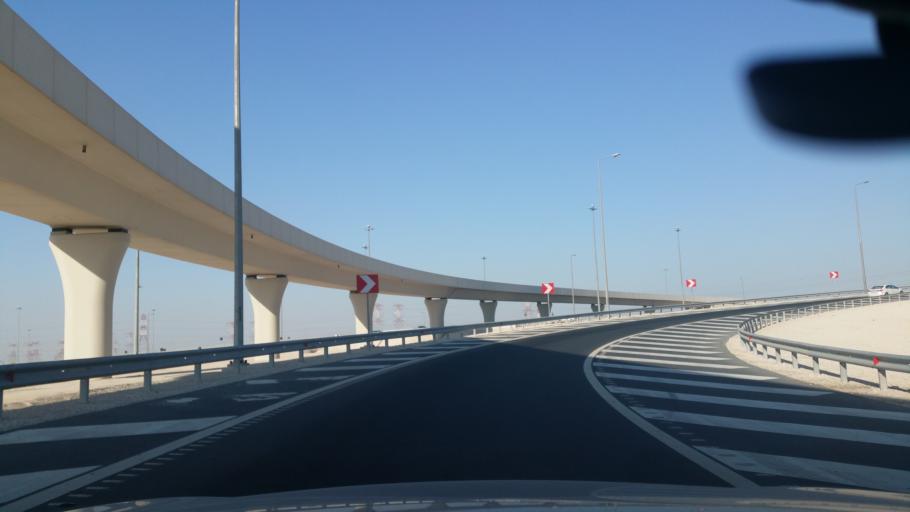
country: QA
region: Baladiyat ar Rayyan
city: Ar Rayyan
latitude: 25.1736
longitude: 51.3247
